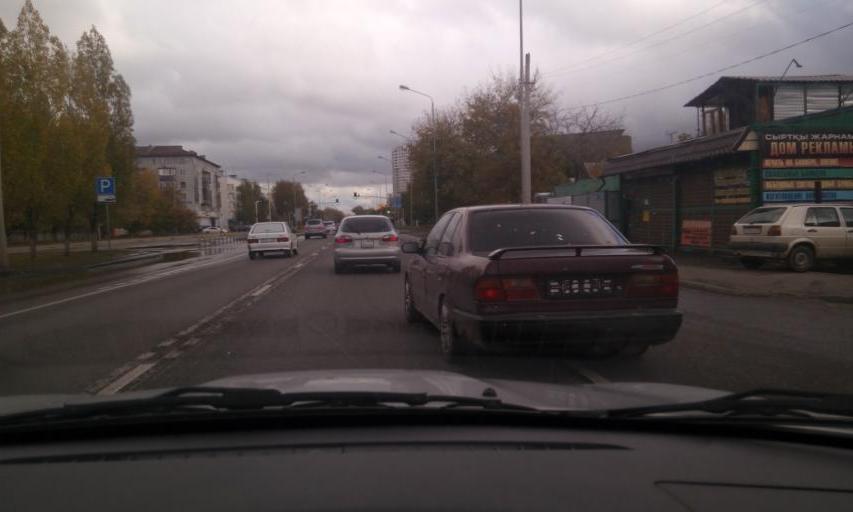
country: KZ
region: Astana Qalasy
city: Astana
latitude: 51.1676
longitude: 71.4583
